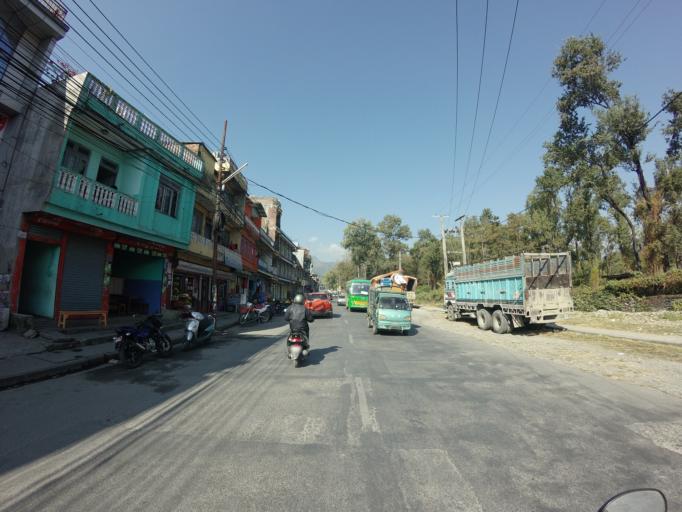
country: NP
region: Western Region
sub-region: Gandaki Zone
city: Pokhara
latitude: 28.2219
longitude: 83.9946
